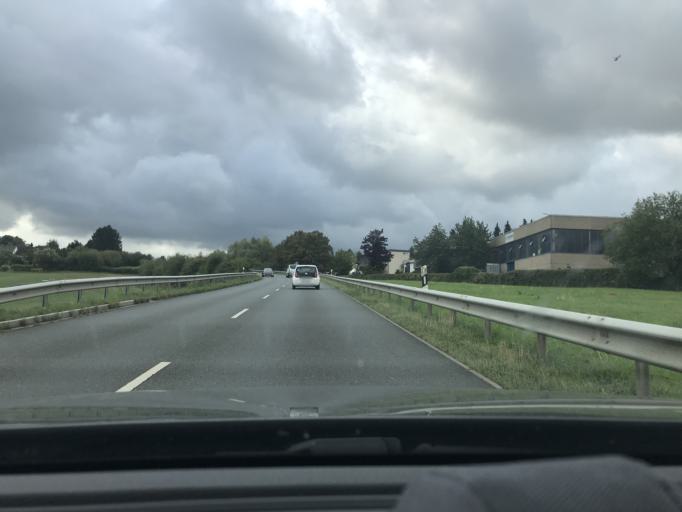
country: DE
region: North Rhine-Westphalia
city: Haan
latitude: 51.2140
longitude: 7.0177
